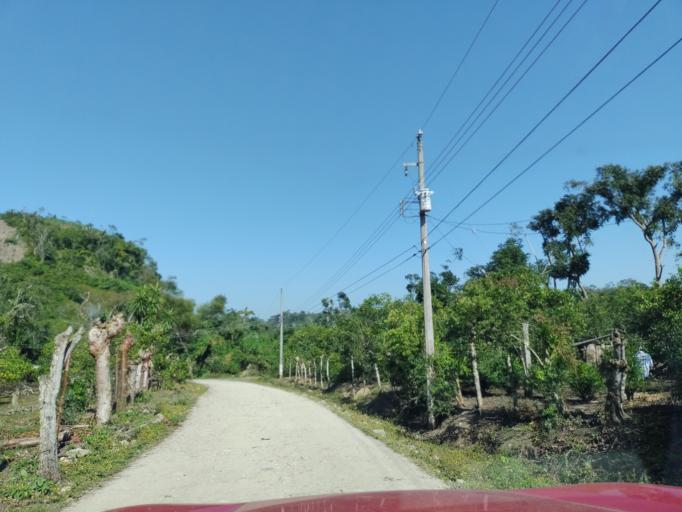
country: MX
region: Veracruz
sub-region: Papantla
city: Polutla
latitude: 20.4918
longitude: -97.1828
